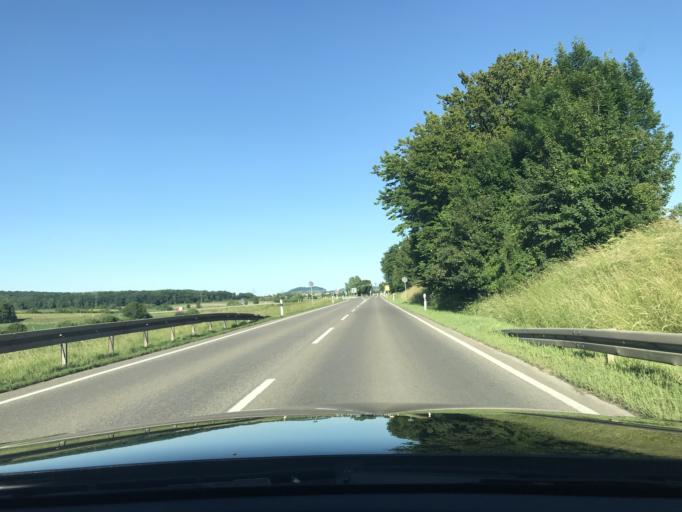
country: DE
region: Baden-Wuerttemberg
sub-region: Regierungsbezirk Stuttgart
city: Stuttgart Muehlhausen
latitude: 48.8477
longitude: 9.2655
